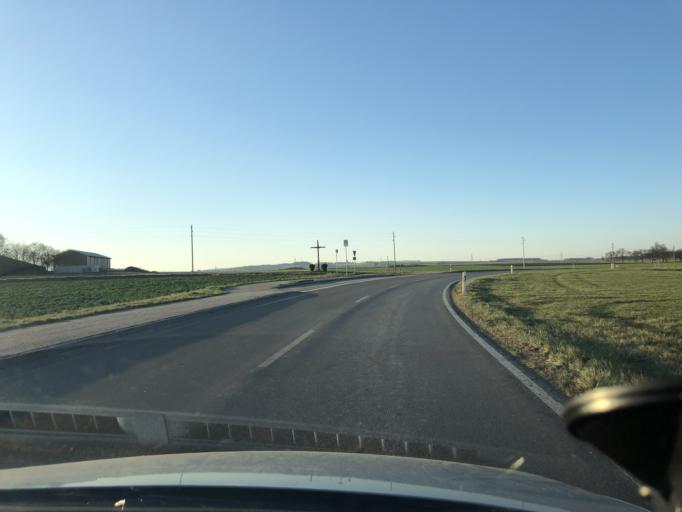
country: DE
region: Baden-Wuerttemberg
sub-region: Freiburg Region
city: Braunlingen
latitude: 47.8725
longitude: 8.4608
